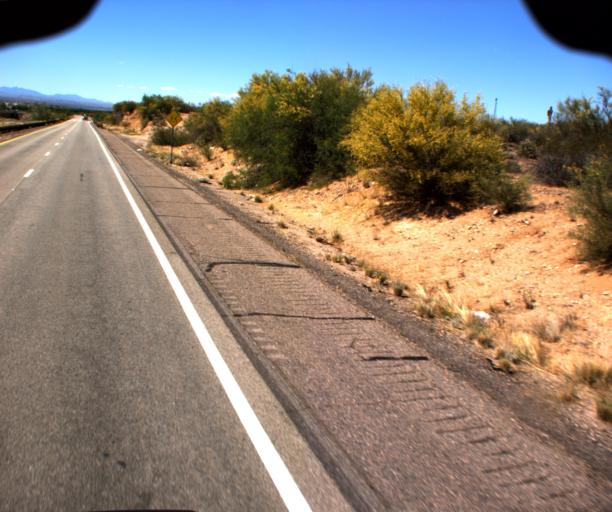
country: US
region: Arizona
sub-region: Yavapai County
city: Bagdad
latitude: 34.6537
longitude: -113.5738
